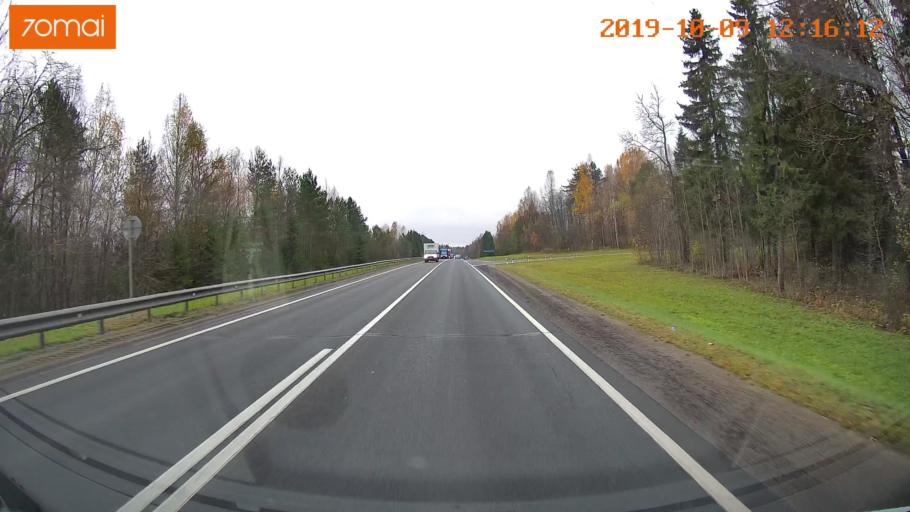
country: RU
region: Jaroslavl
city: Prechistoye
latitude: 58.4720
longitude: 40.3215
